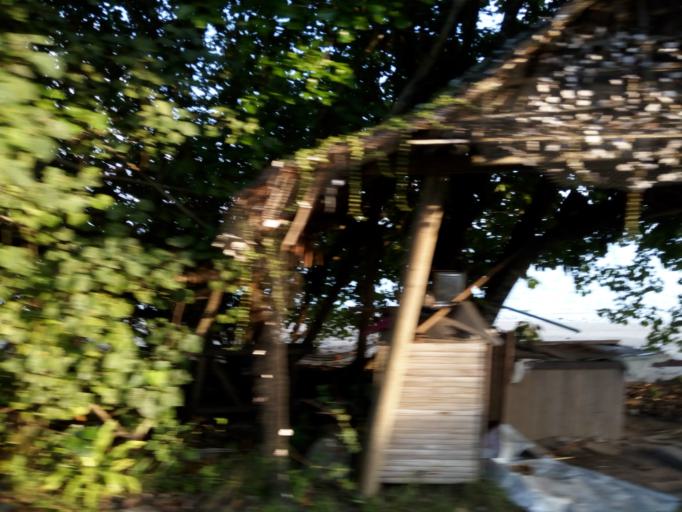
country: TH
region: Phangnga
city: Ko Yao
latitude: 8.1007
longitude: 98.6205
